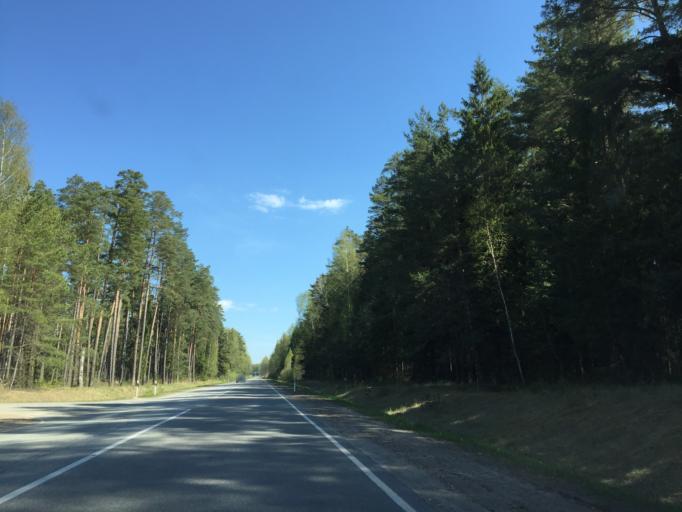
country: LV
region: Saulkrastu
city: Saulkrasti
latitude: 57.3245
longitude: 24.4298
